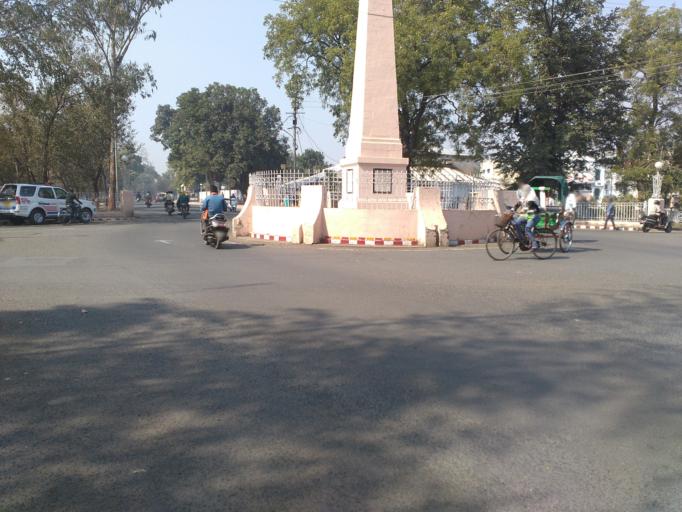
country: IN
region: Madhya Pradesh
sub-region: Jabalpur
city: Jabalpur
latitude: 23.1565
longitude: 79.9475
